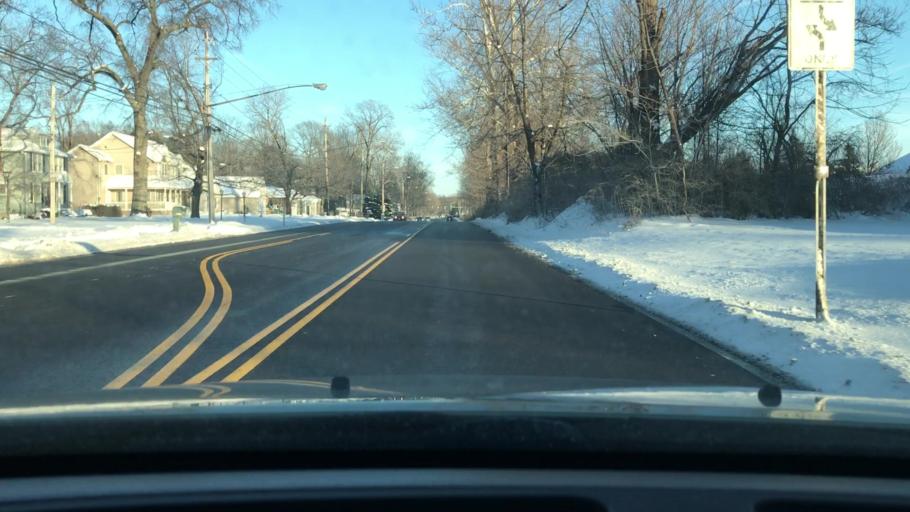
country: US
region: Ohio
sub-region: Lake County
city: Mentor
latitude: 41.6591
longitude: -81.3456
